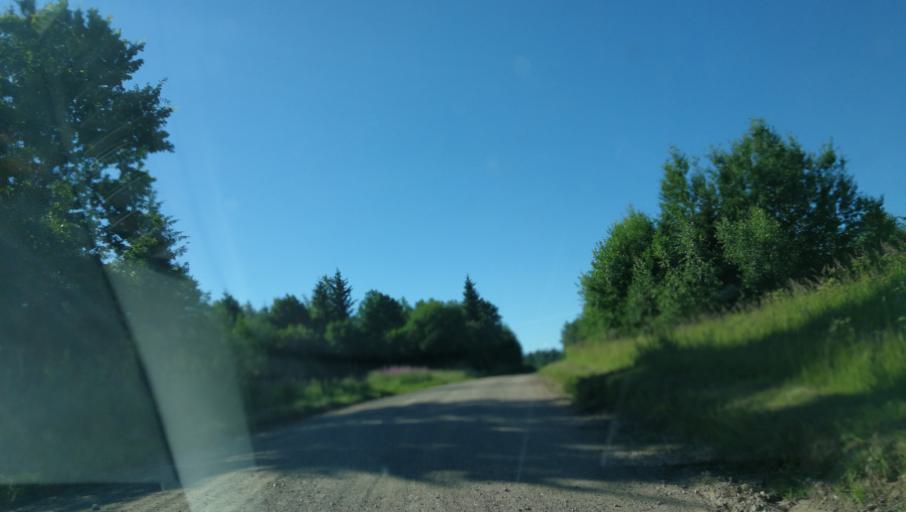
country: LV
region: Jaunpiebalga
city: Jaunpiebalga
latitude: 57.0230
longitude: 26.0324
